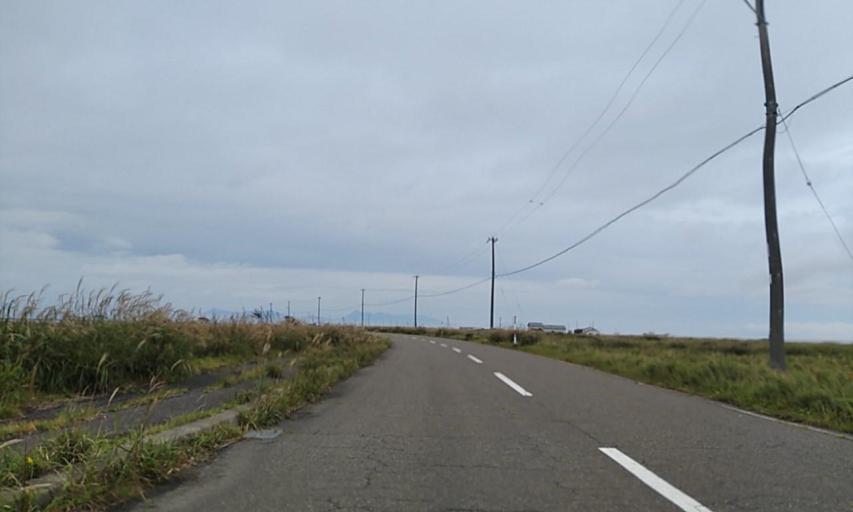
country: JP
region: Hokkaido
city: Shibetsu
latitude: 43.5688
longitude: 145.3466
